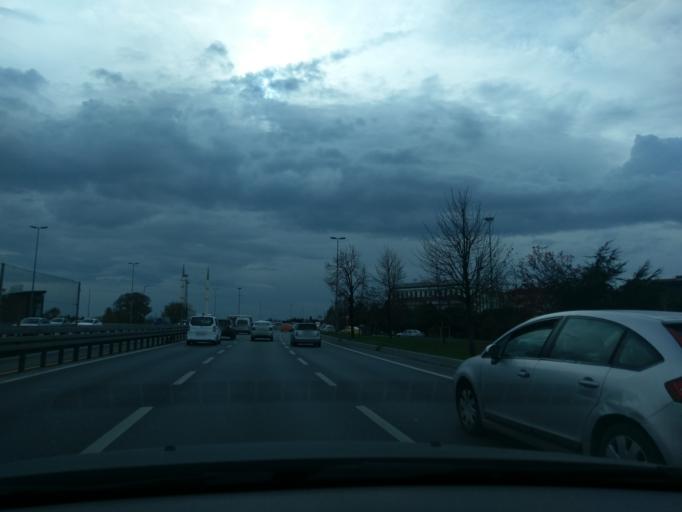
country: TR
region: Istanbul
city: Bahcelievler
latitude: 40.9915
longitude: 28.7938
